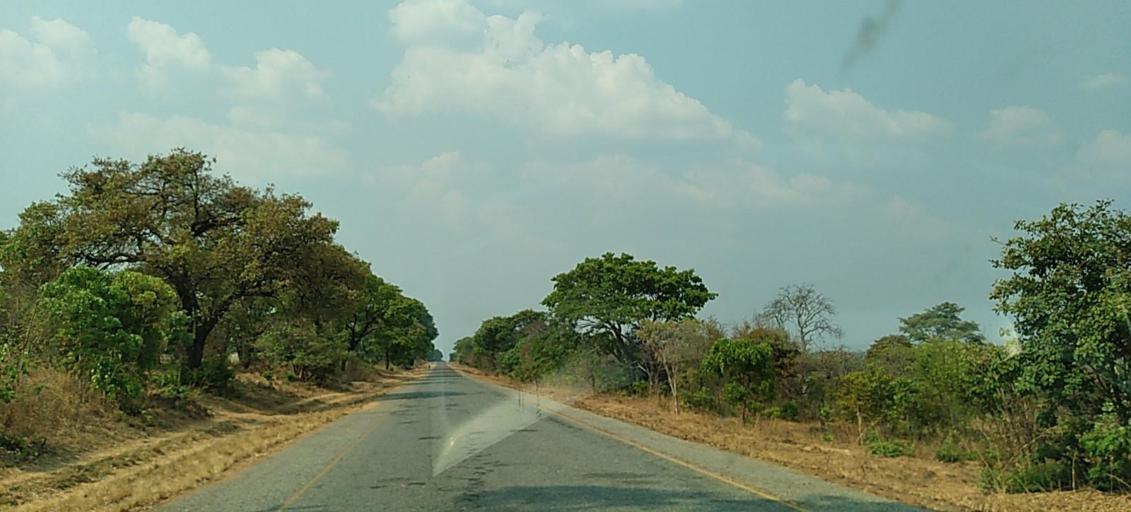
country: ZM
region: North-Western
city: Kabompo
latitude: -13.6302
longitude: 24.1096
